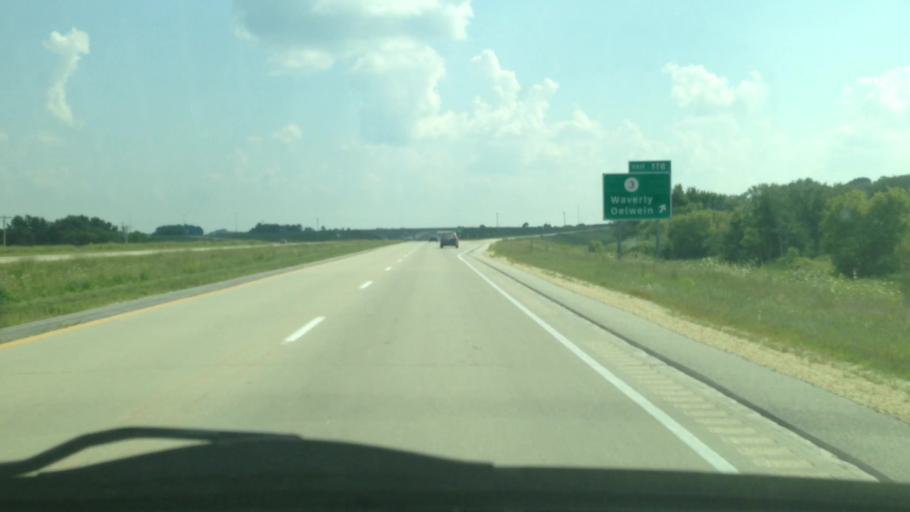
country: US
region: Iowa
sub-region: Bremer County
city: Denver
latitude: 42.7204
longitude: -92.3374
